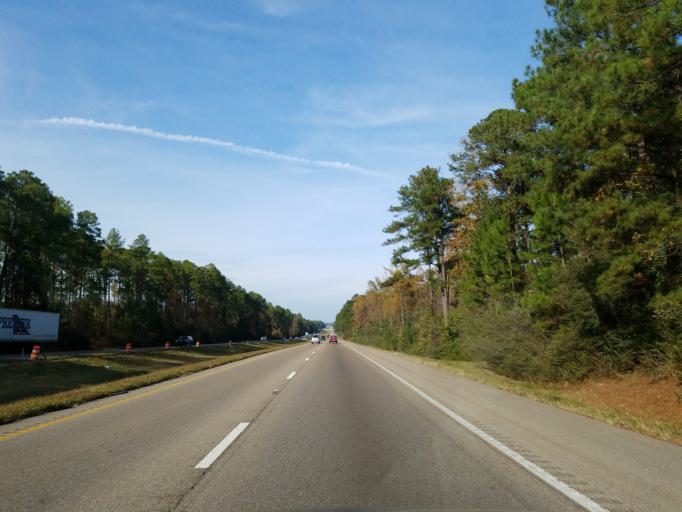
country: US
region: Mississippi
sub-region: Lamar County
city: West Hattiesburg
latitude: 31.2904
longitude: -89.3526
